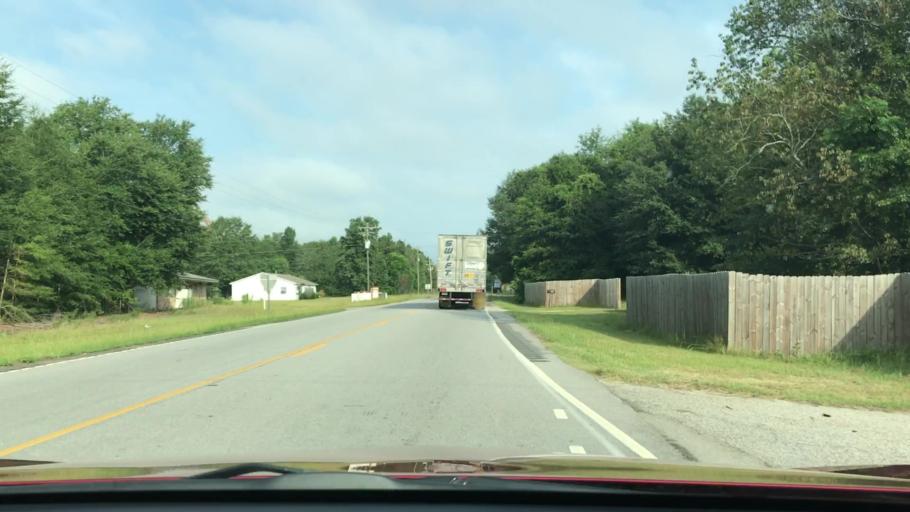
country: US
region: South Carolina
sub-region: Barnwell County
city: Williston
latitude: 33.6348
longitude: -81.3187
